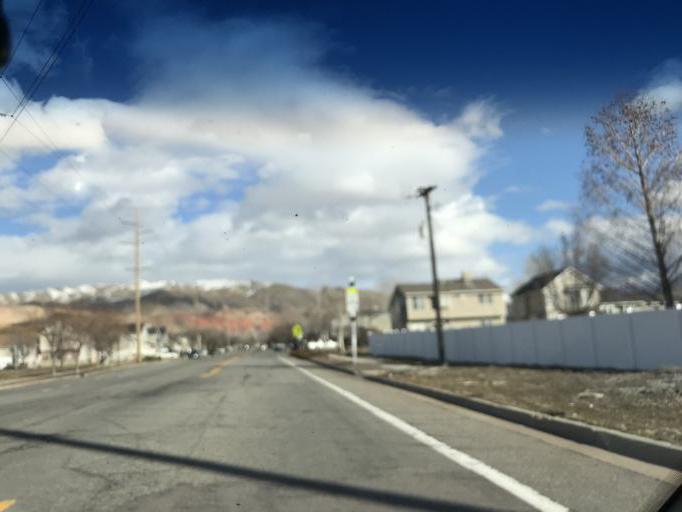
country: US
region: Utah
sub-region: Davis County
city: North Salt Lake
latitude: 40.8056
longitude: -111.9454
